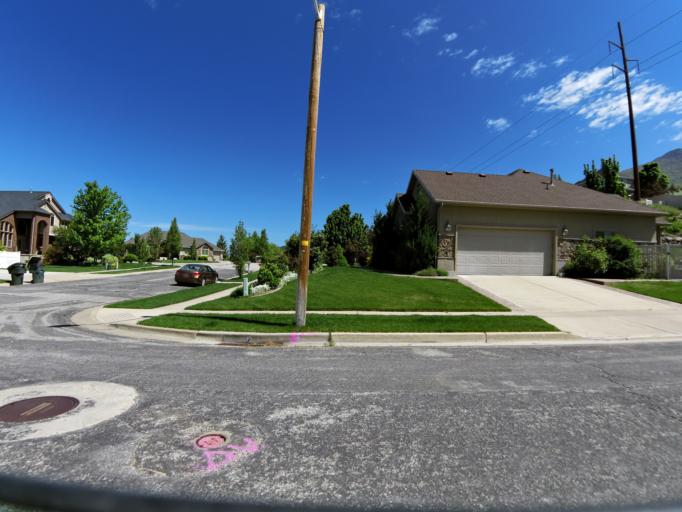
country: US
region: Utah
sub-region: Weber County
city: Uintah
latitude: 41.1747
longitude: -111.9403
